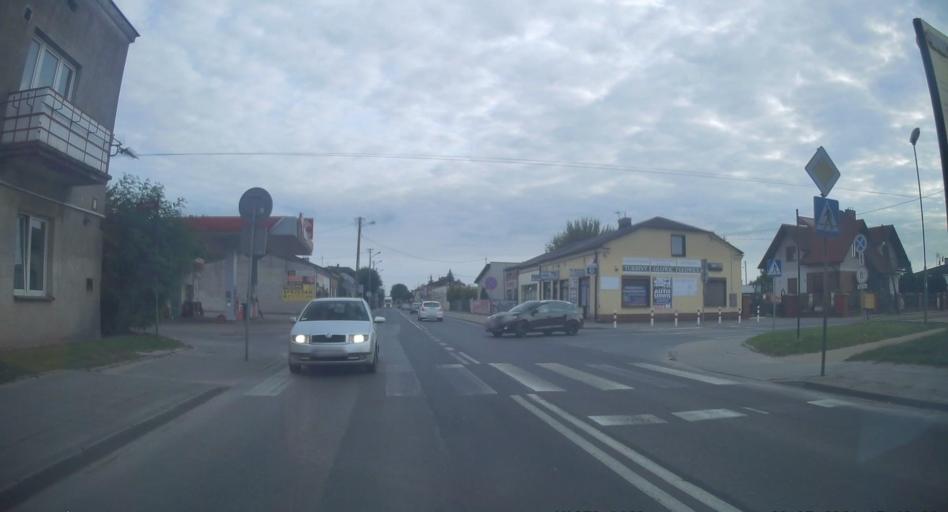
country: PL
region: Lodz Voivodeship
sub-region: Powiat radomszczanski
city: Radomsko
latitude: 51.0795
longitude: 19.4504
